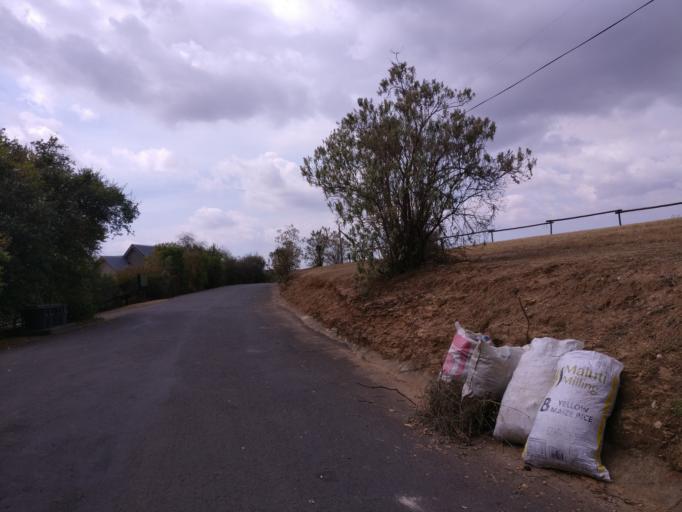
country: ZA
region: KwaZulu-Natal
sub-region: uThukela District Municipality
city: Bergville
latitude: -29.0143
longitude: 29.4199
